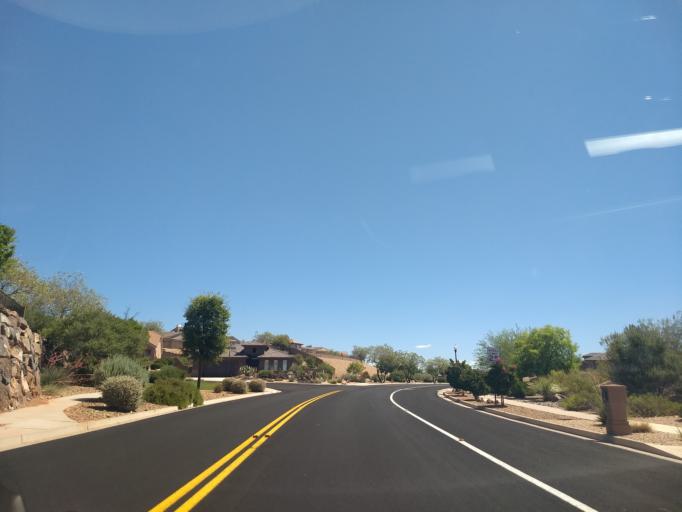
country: US
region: Utah
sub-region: Washington County
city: Washington
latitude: 37.1427
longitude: -113.4655
